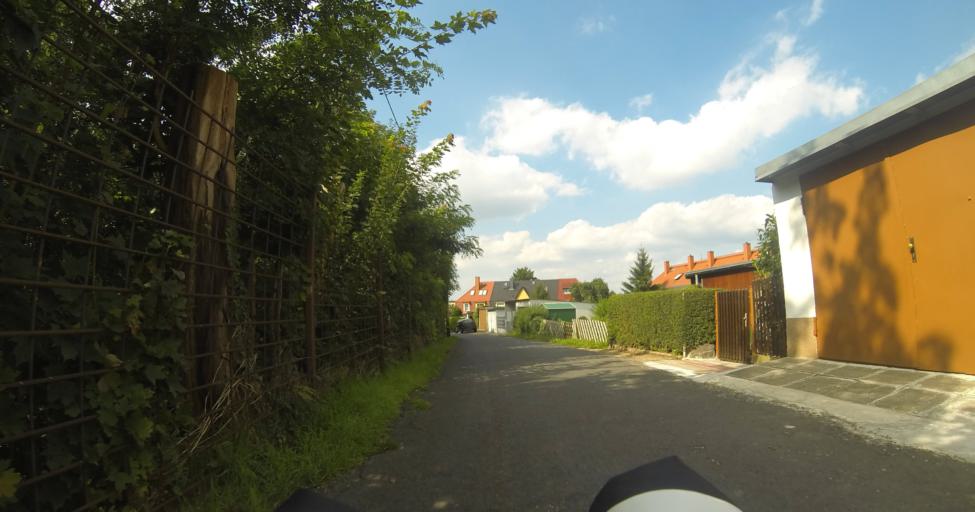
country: DE
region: Saxony
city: Grossenhain
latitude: 51.2848
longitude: 13.5331
